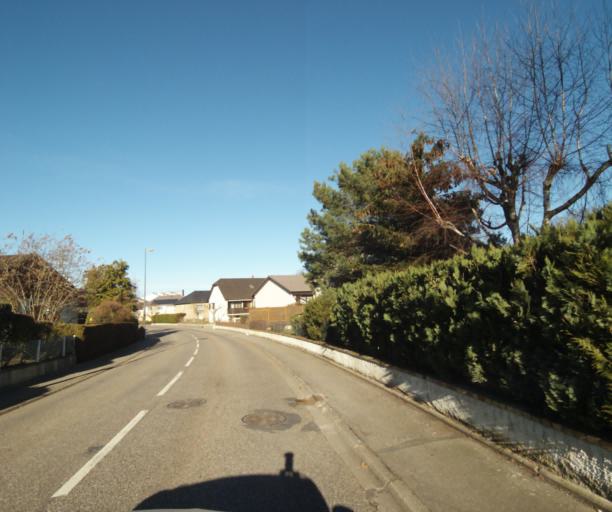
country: FR
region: Lorraine
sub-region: Departement de Meurthe-et-Moselle
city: Fleville-devant-Nancy
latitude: 48.6415
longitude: 6.1996
